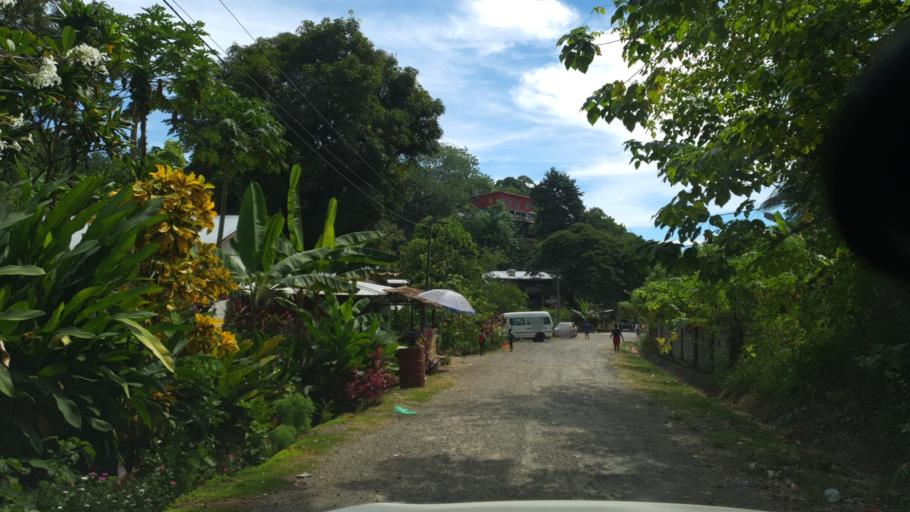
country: SB
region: Guadalcanal
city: Honiara
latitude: -9.4304
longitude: 159.9323
